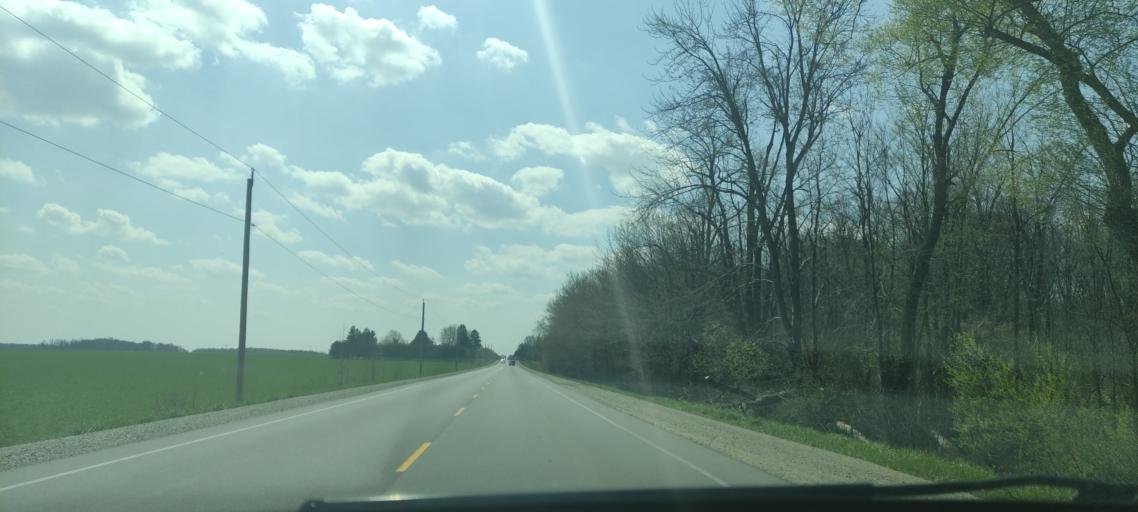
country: CA
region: Ontario
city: Stratford
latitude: 43.3399
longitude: -80.9979
